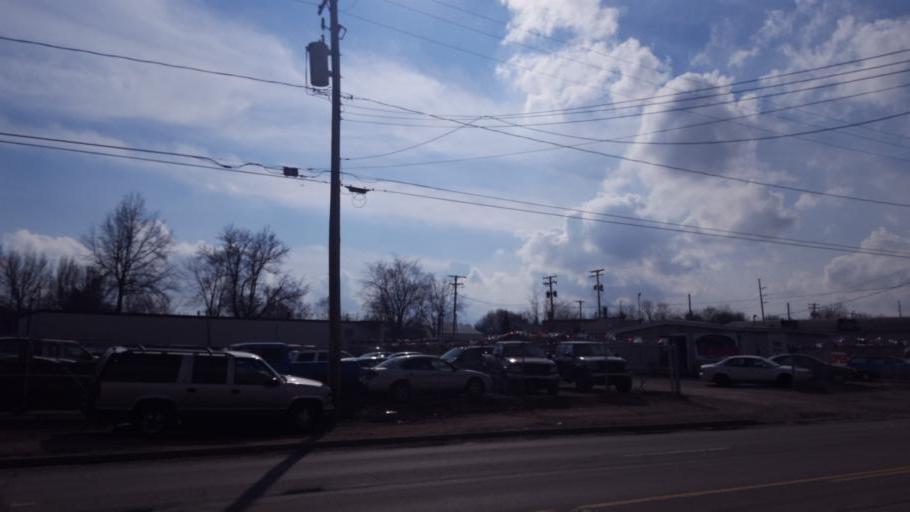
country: US
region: Ohio
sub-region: Richland County
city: Mansfield
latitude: 40.7844
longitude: -82.5501
